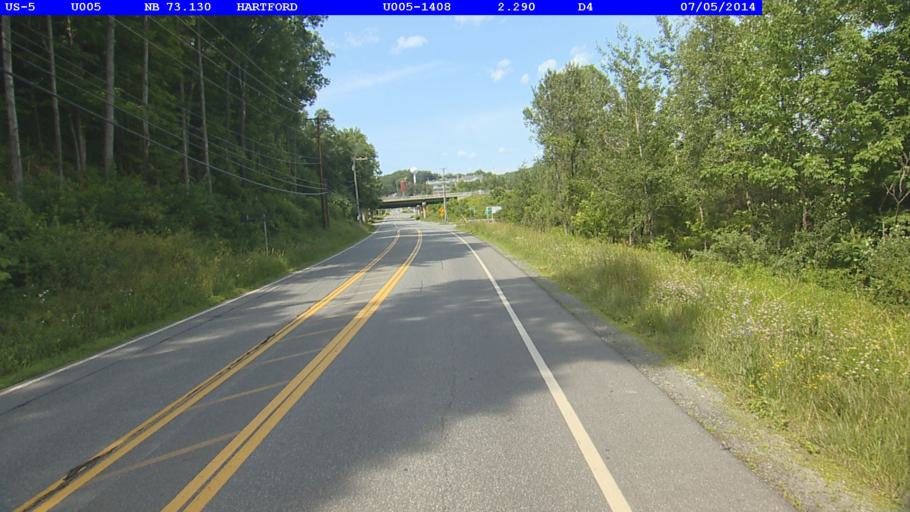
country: US
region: Vermont
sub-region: Windsor County
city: White River Junction
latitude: 43.6427
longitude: -72.3464
